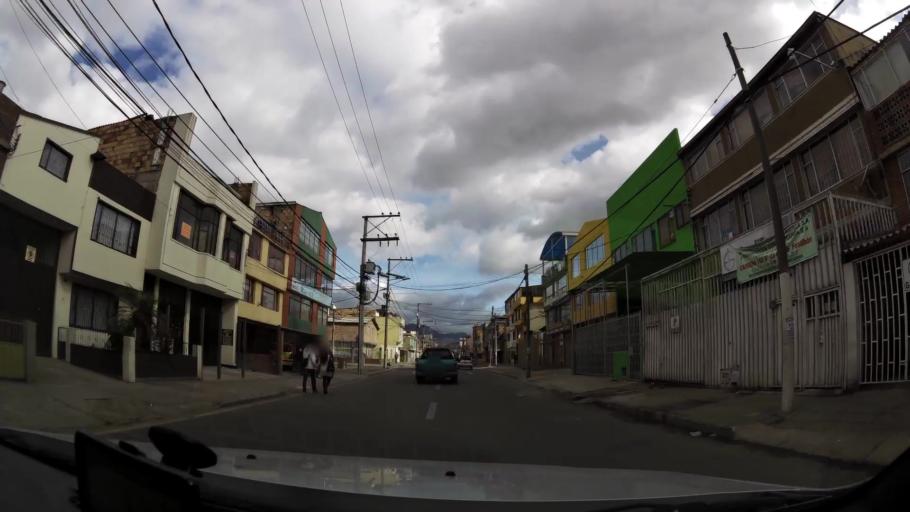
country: CO
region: Bogota D.C.
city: Bogota
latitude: 4.6144
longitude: -74.1385
